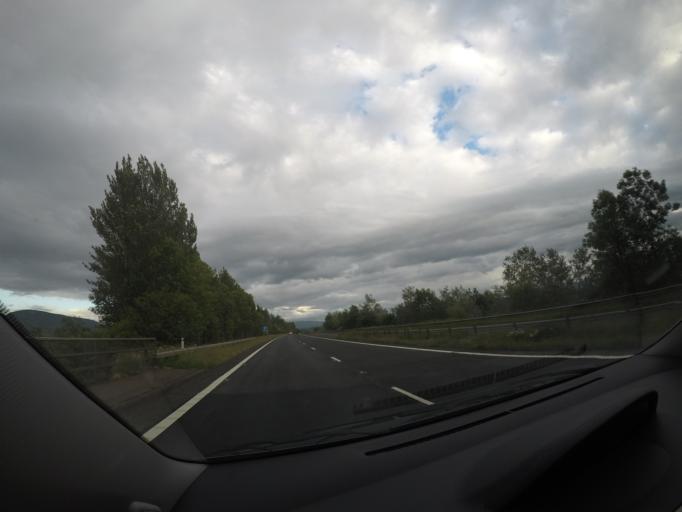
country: GB
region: England
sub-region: Cumbria
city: Appleby-in-Westmorland
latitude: 54.5768
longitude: -2.4702
